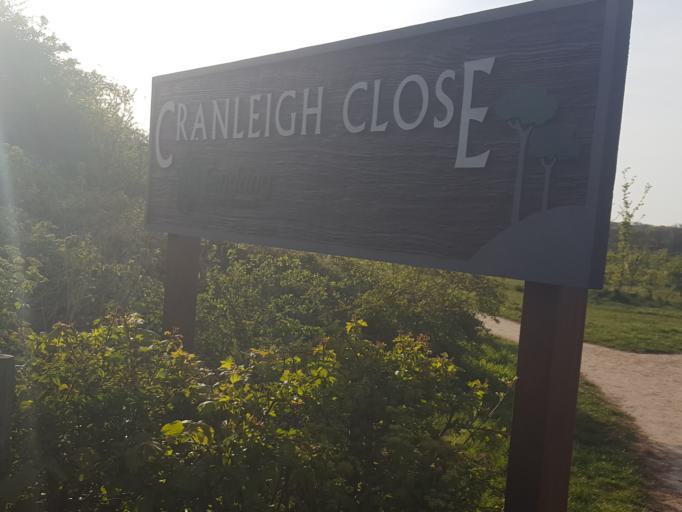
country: GB
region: England
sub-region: Essex
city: Little Clacton
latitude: 51.8078
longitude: 1.1304
